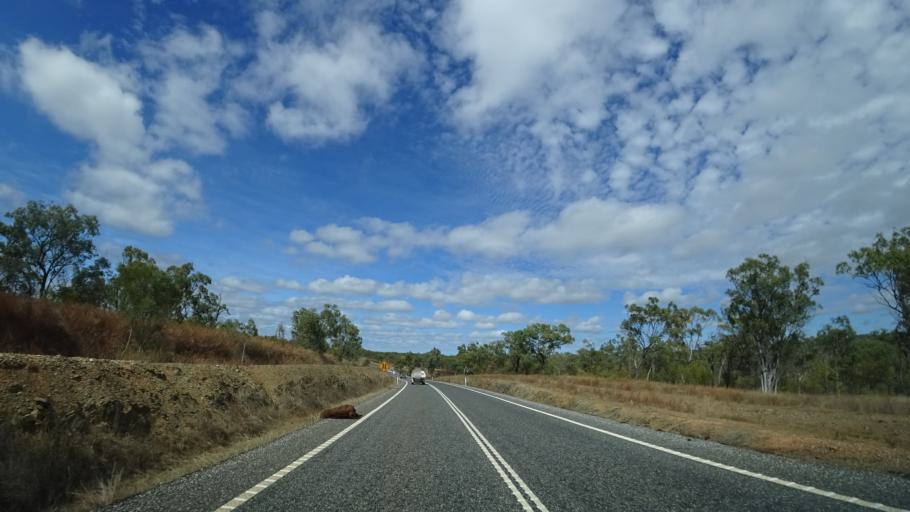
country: AU
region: Queensland
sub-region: Cairns
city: Port Douglas
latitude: -16.3845
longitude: 144.7365
